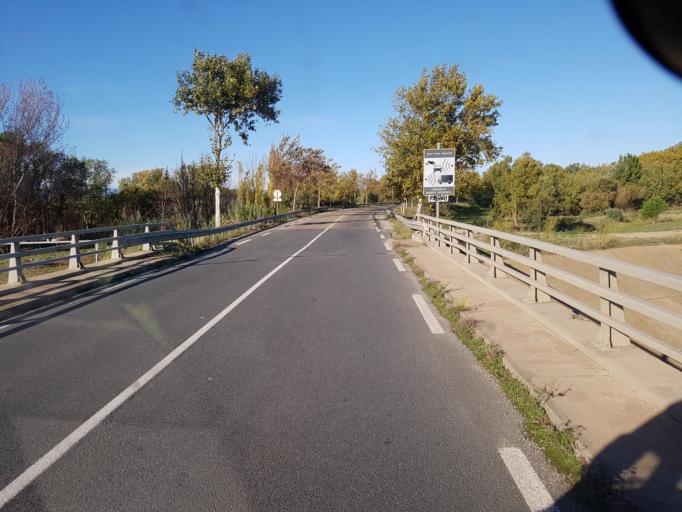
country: FR
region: Languedoc-Roussillon
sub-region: Departement de l'Aude
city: Coursan
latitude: 43.2397
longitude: 3.0597
